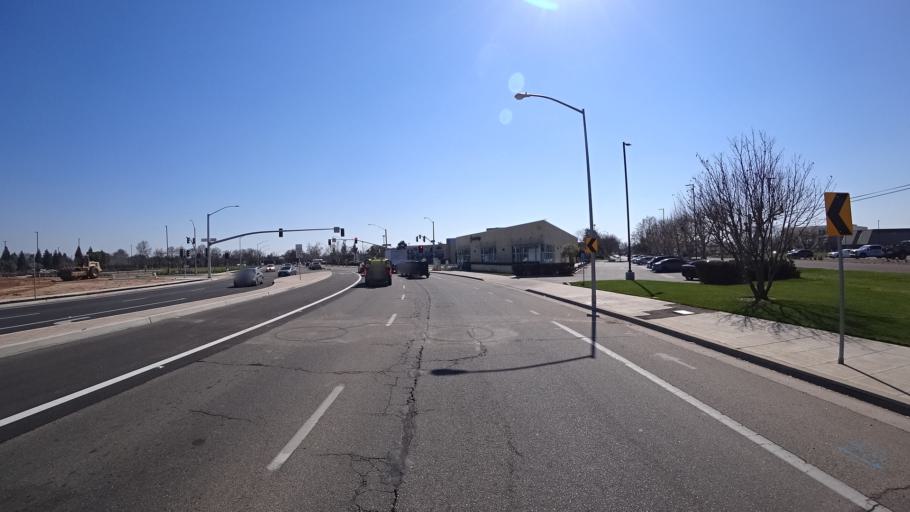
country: US
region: California
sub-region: Fresno County
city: Clovis
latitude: 36.8407
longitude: -119.7567
